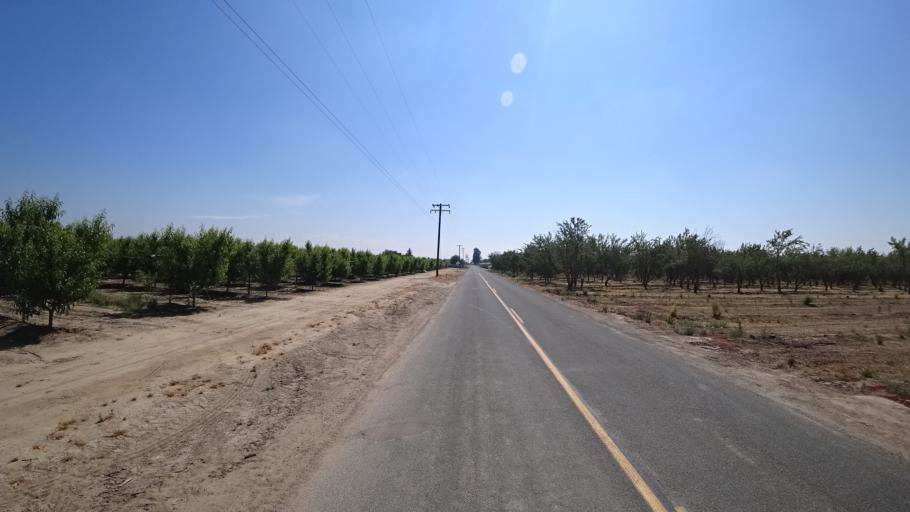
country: US
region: California
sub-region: Fresno County
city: Kingsburg
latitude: 36.4524
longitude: -119.5641
